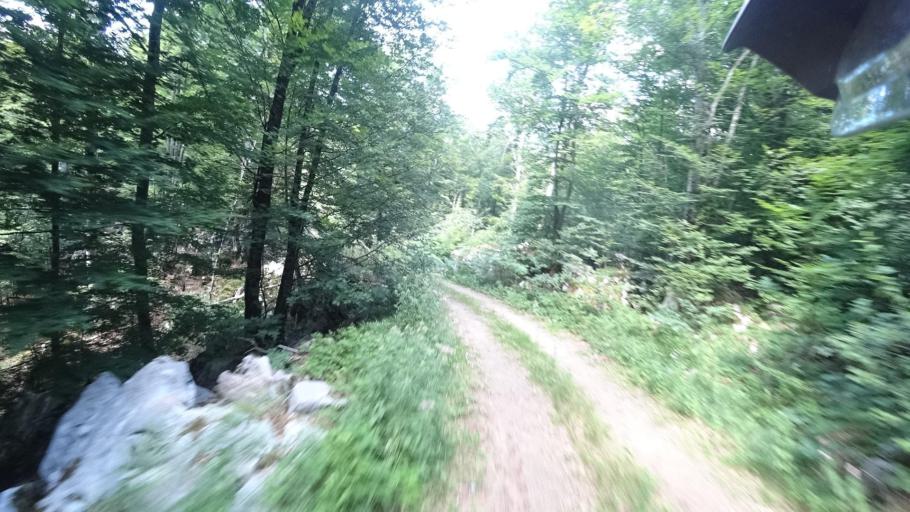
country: HR
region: Licko-Senjska
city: Brinje
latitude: 45.1275
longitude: 15.1275
